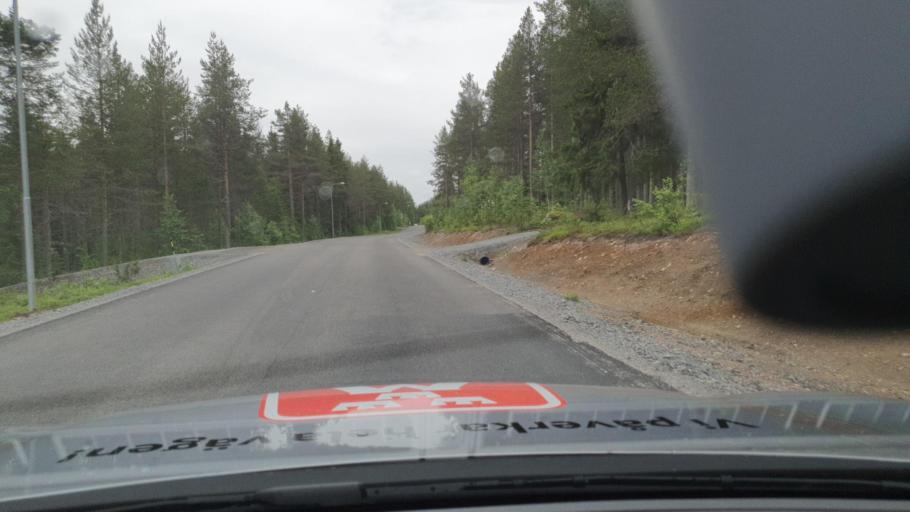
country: SE
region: Norrbotten
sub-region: Overtornea Kommun
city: OEvertornea
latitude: 66.6140
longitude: 23.2918
